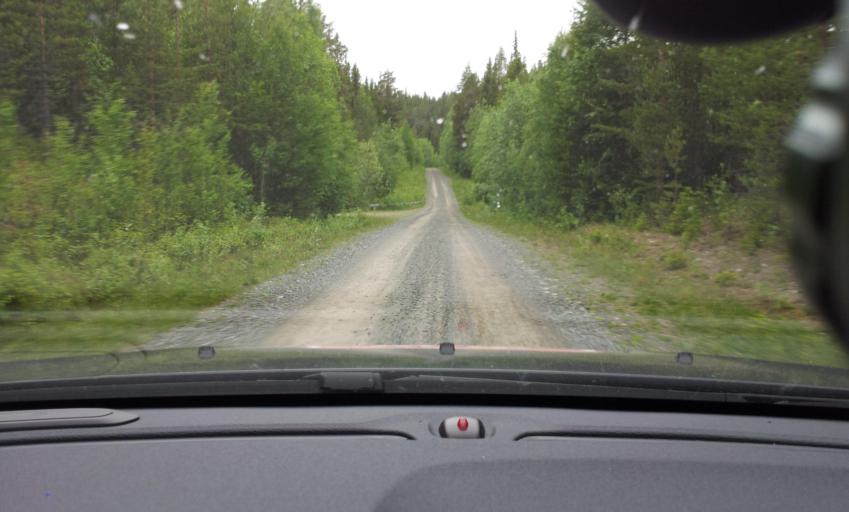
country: SE
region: Jaemtland
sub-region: Are Kommun
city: Jarpen
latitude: 63.1693
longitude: 13.5836
